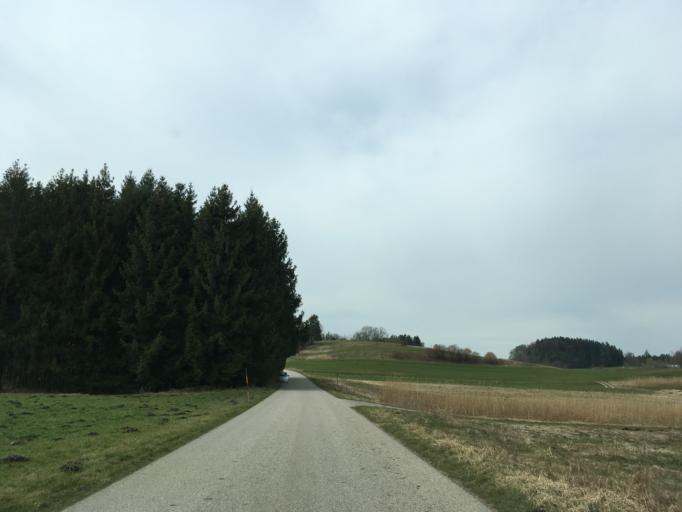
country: DE
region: Bavaria
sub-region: Upper Bavaria
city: Eggstatt
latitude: 47.9446
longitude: 12.3862
